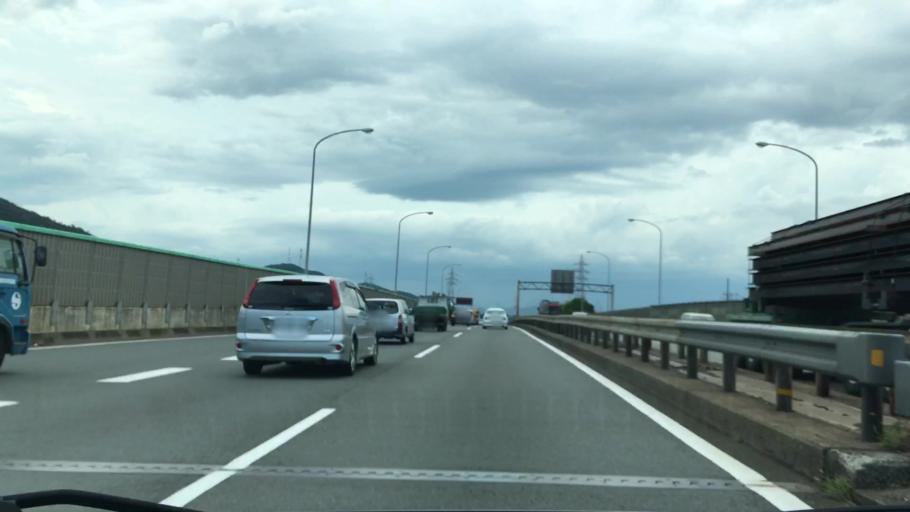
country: JP
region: Hyogo
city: Shirahamacho-usazakiminami
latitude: 34.7913
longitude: 134.7679
